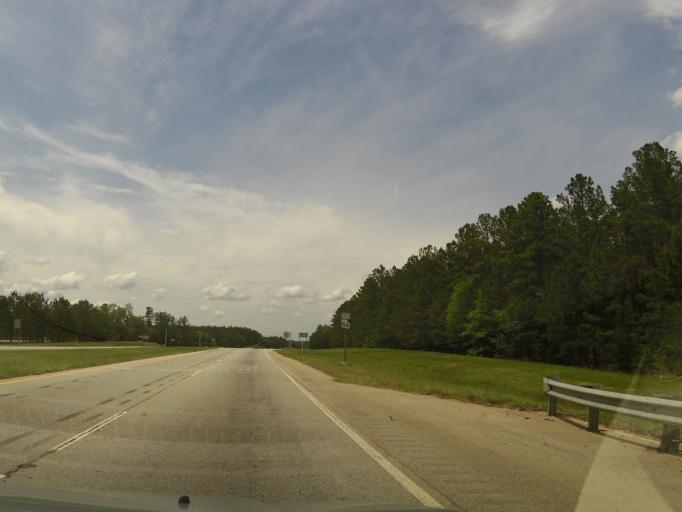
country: US
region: Georgia
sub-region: Emanuel County
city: Swainsboro
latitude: 32.5744
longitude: -82.3570
